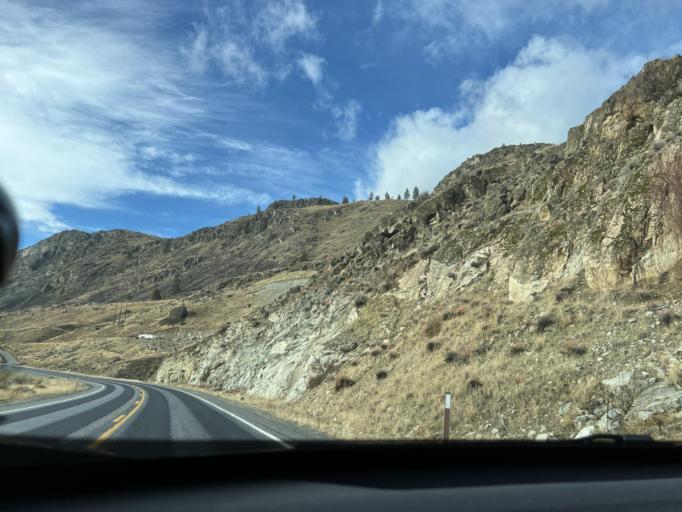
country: US
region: Washington
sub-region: Chelan County
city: Chelan
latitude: 47.8540
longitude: -119.9628
